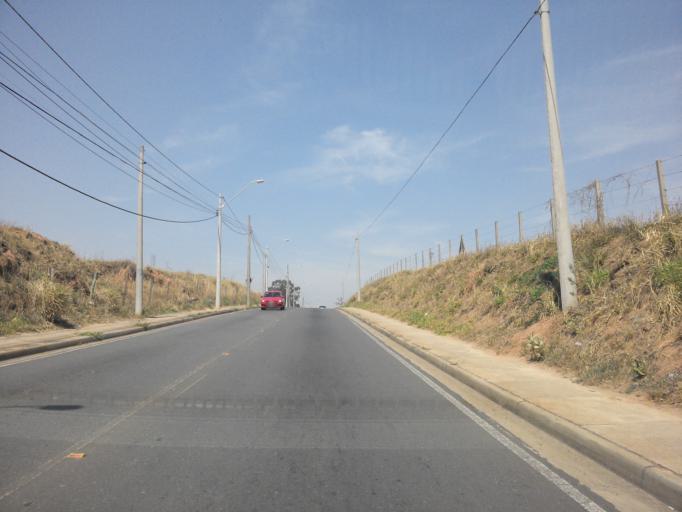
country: BR
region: Sao Paulo
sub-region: Hortolandia
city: Hortolandia
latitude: -22.9340
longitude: -47.1872
